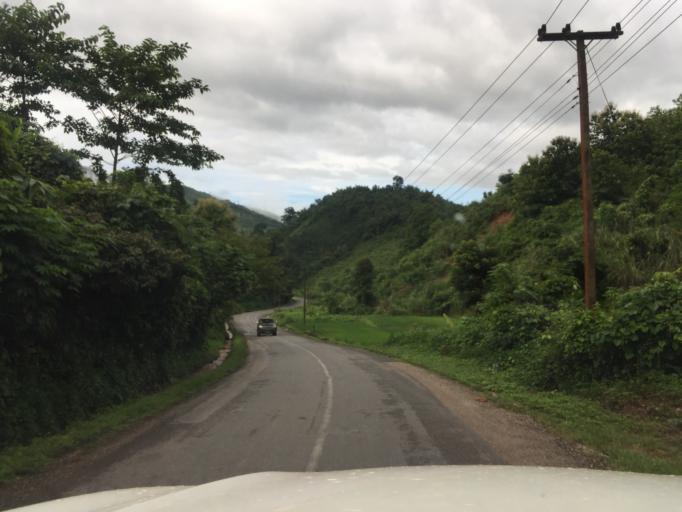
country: LA
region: Oudomxai
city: Muang La
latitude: 20.7992
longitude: 102.0863
